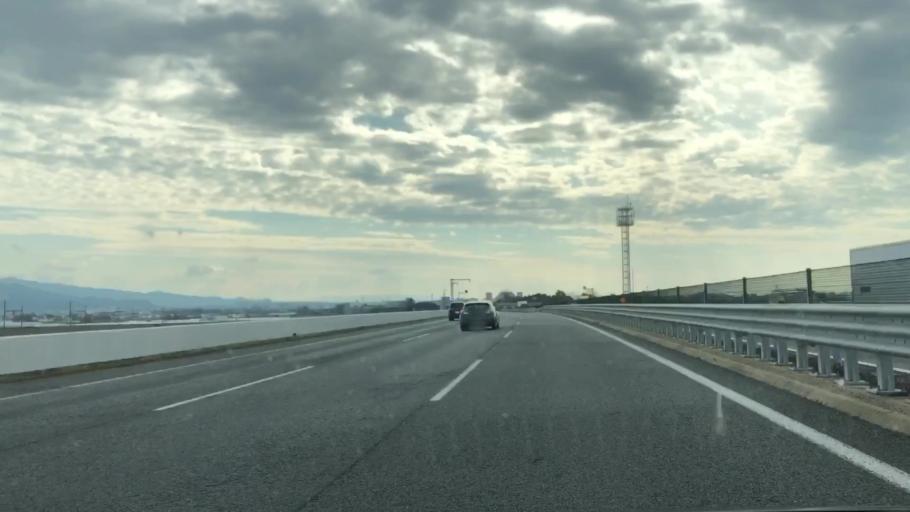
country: JP
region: Saga Prefecture
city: Tosu
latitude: 33.3541
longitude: 130.5381
